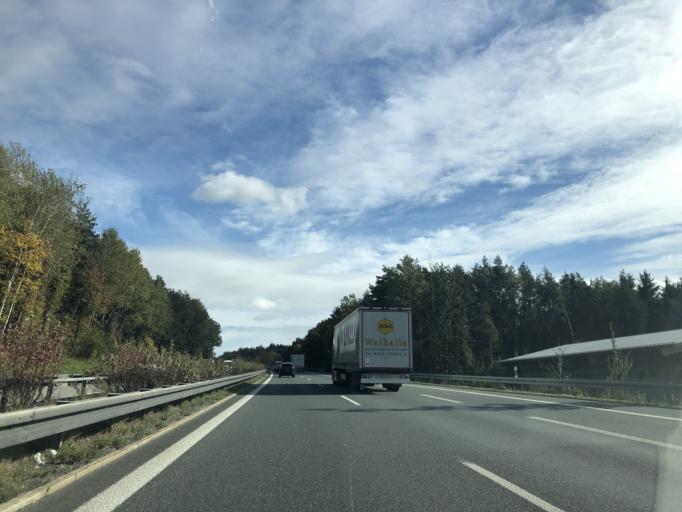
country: DE
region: Bavaria
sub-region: Upper Palatinate
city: Pilsach
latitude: 49.3155
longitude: 11.4783
